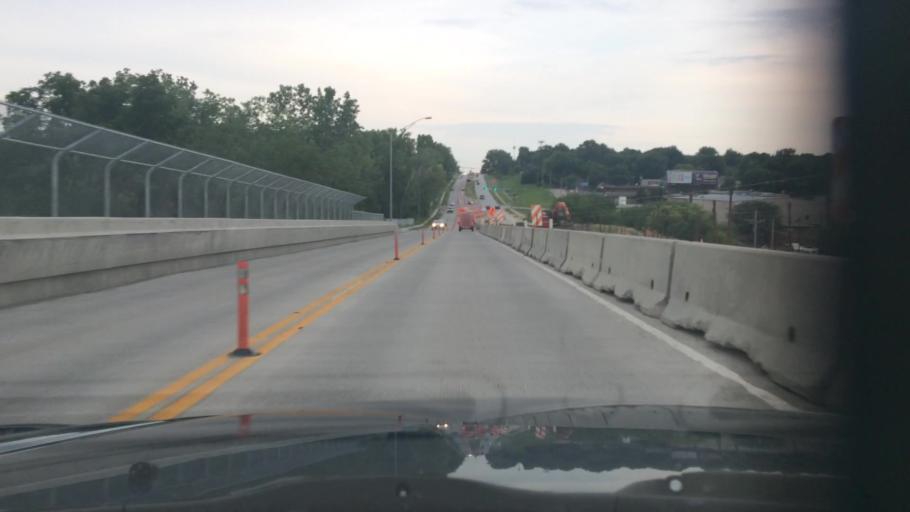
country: US
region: Nebraska
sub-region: Douglas County
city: Ralston
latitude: 41.1985
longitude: -96.0430
